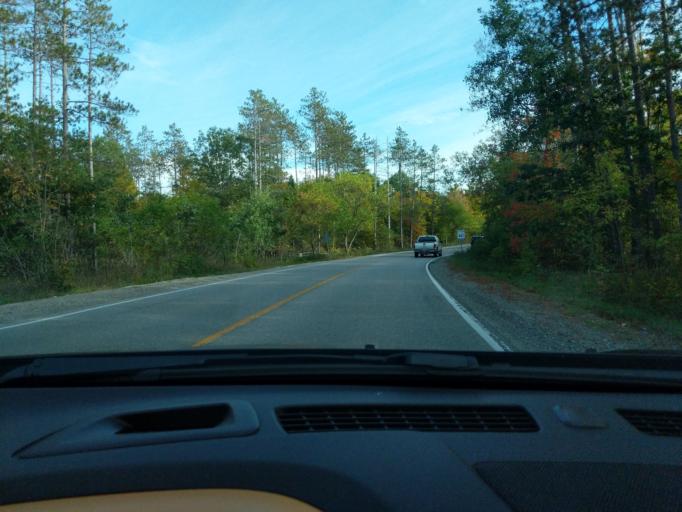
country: CA
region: Ontario
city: Barrie
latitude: 44.4299
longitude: -79.7660
